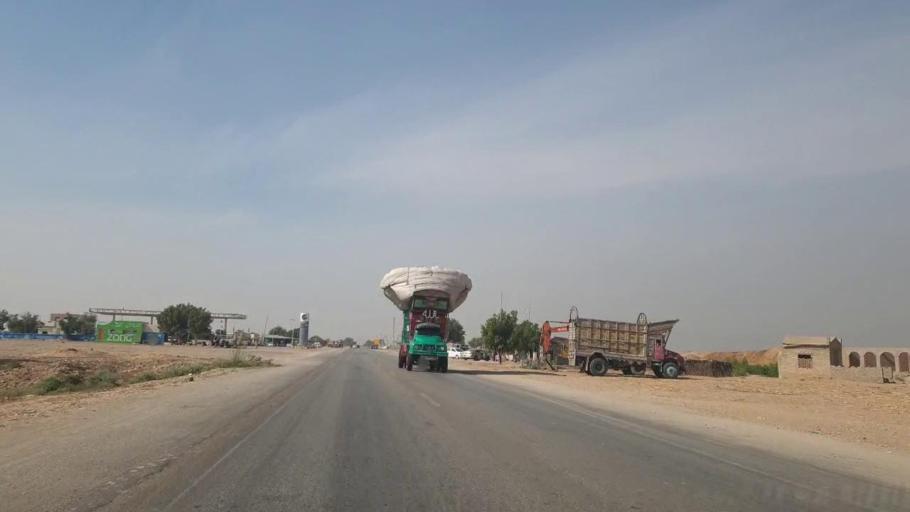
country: PK
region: Sindh
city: Sann
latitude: 26.0269
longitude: 68.1268
